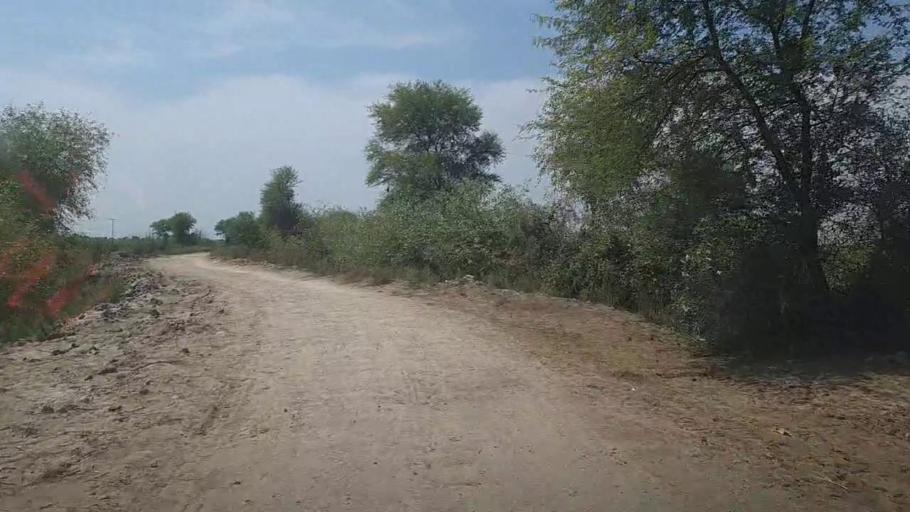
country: PK
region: Sindh
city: Kandhkot
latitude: 28.3091
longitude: 69.2416
